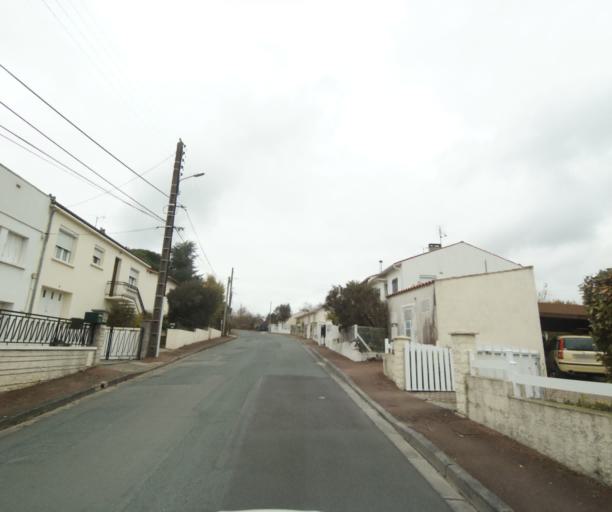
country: FR
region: Poitou-Charentes
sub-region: Departement de la Charente-Maritime
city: Fontcouverte
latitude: 45.7469
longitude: -0.6029
